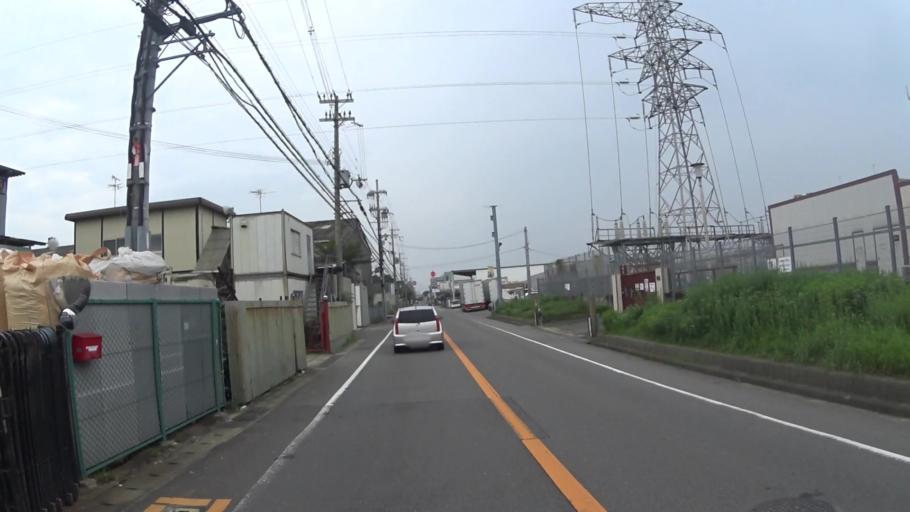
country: JP
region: Kyoto
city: Tanabe
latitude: 34.8574
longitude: 135.7451
